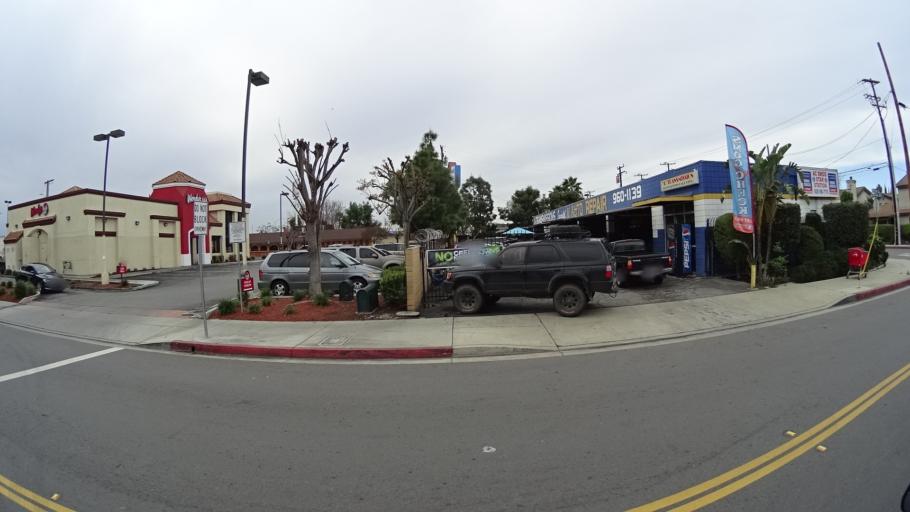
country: US
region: California
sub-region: Los Angeles County
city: West Puente Valley
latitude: 34.0700
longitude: -117.9802
